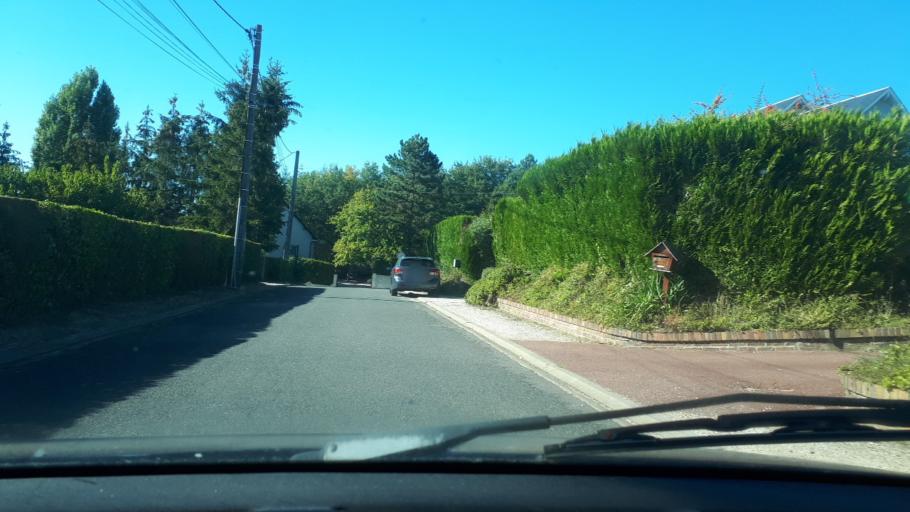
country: FR
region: Centre
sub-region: Departement du Loir-et-Cher
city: Villiers-sur-Loir
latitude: 47.8074
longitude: 0.9985
